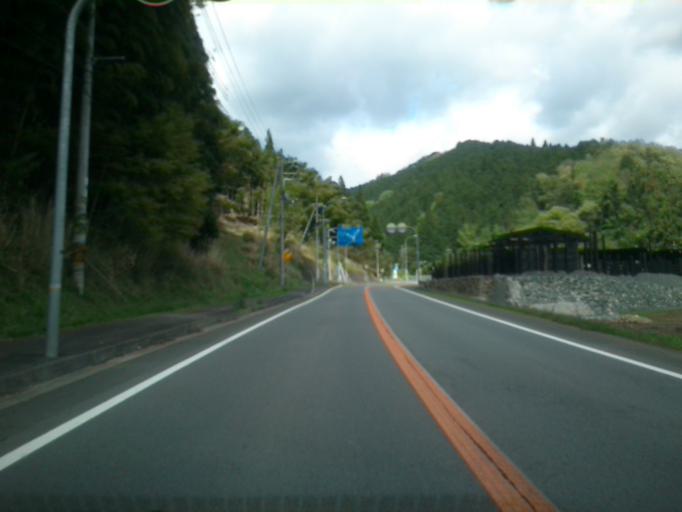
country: JP
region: Kyoto
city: Fukuchiyama
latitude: 35.4220
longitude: 135.0253
